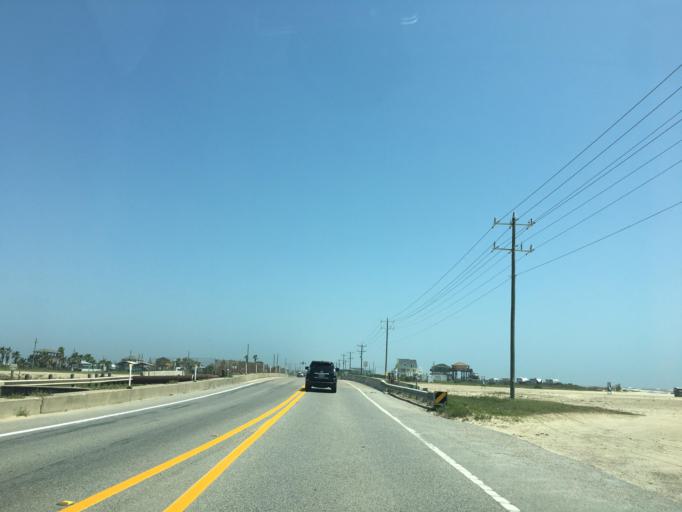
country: US
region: Texas
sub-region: Galveston County
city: Bolivar Peninsula
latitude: 29.5081
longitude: -94.5011
